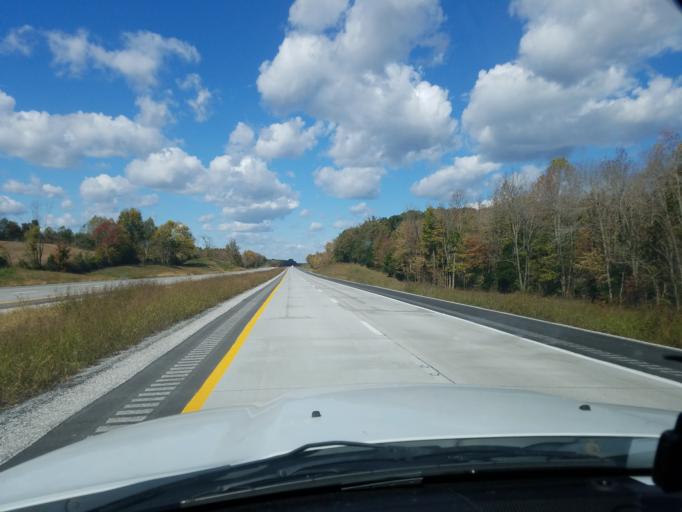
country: US
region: Kentucky
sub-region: Ohio County
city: Oak Grove
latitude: 37.3586
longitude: -86.7915
